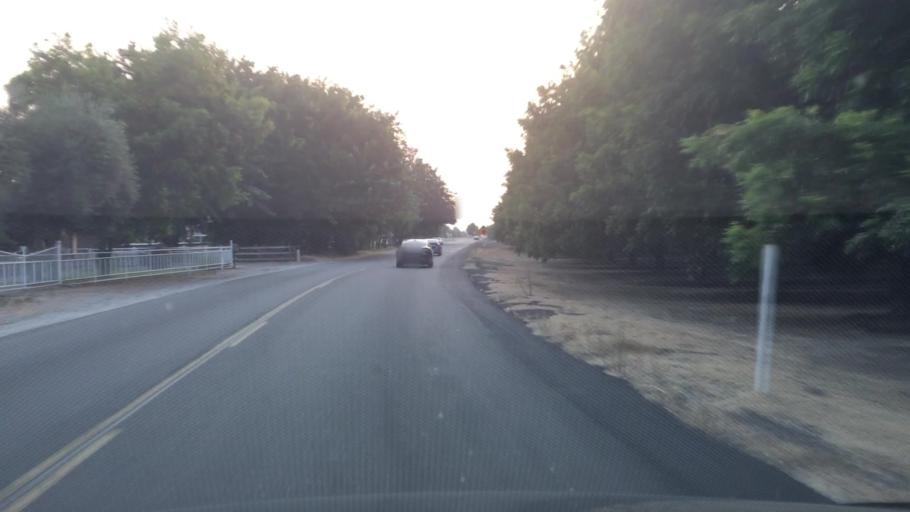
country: US
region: California
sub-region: Fresno County
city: Clovis
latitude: 36.8666
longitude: -119.6900
